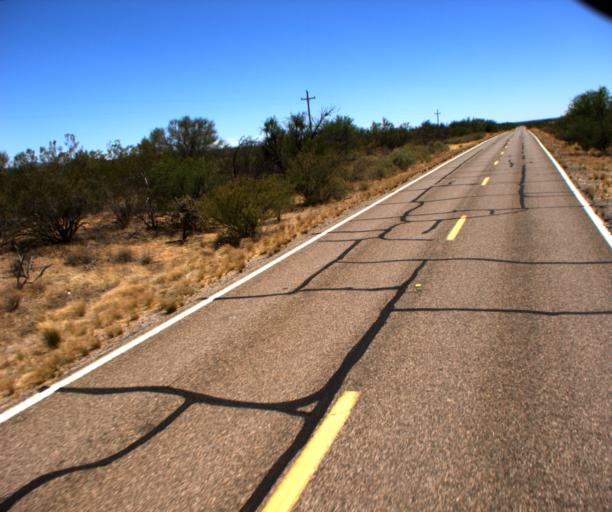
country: US
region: Arizona
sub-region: Pima County
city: Three Points
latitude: 31.9687
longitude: -111.3828
